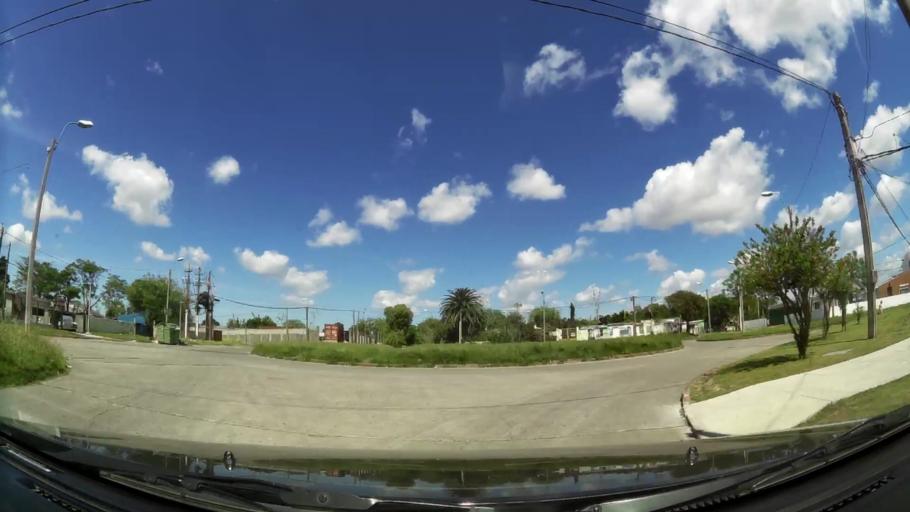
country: UY
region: Montevideo
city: Montevideo
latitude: -34.8394
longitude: -56.1350
